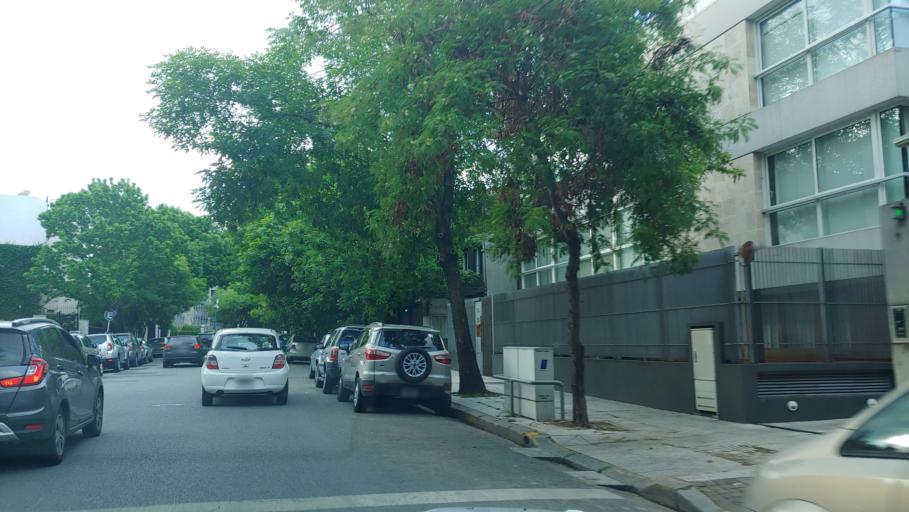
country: AR
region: Buenos Aires F.D.
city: Colegiales
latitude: -34.5713
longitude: -58.4599
